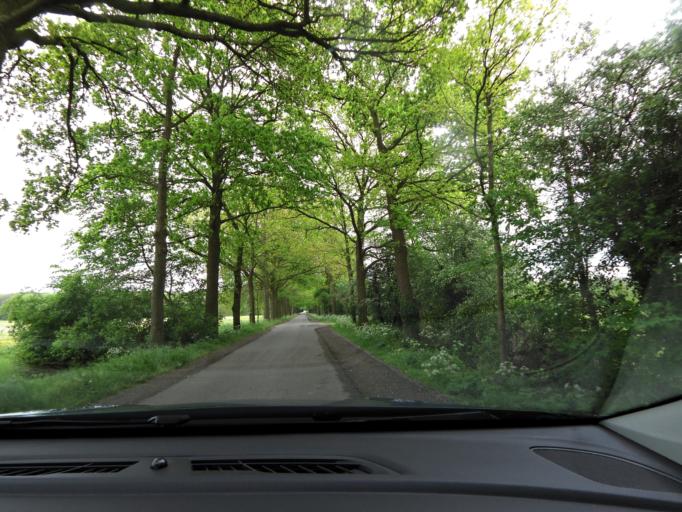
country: NL
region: Gelderland
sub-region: Gemeente Culemborg
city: Culemborg
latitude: 51.8918
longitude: 5.2143
